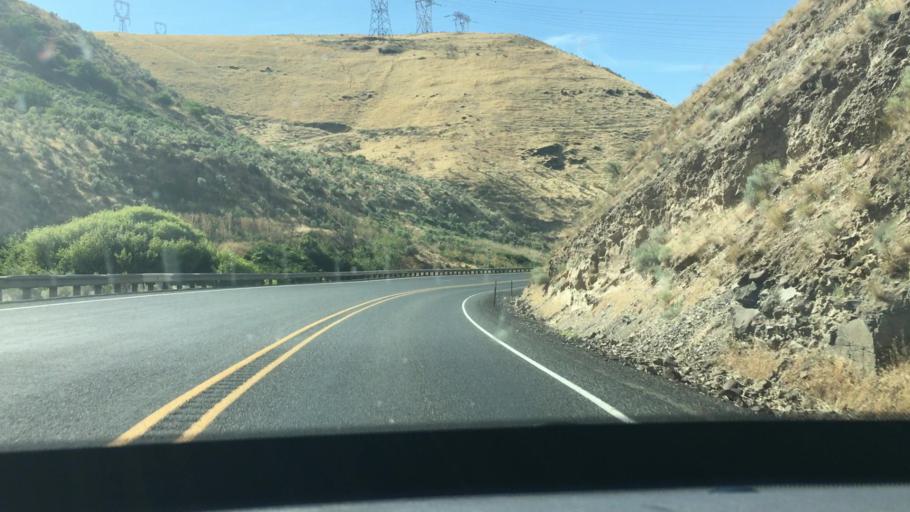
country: US
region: Washington
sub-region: Klickitat County
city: Goldendale
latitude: 45.6499
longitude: -120.8146
